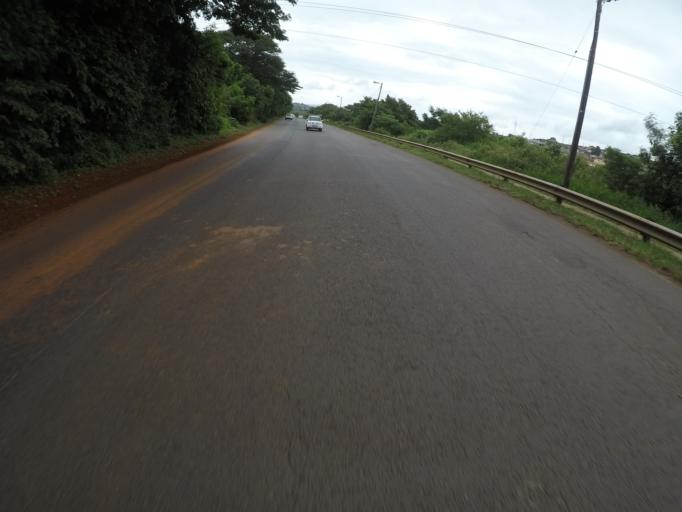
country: ZA
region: KwaZulu-Natal
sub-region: uThungulu District Municipality
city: Empangeni
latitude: -28.7759
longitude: 31.8869
